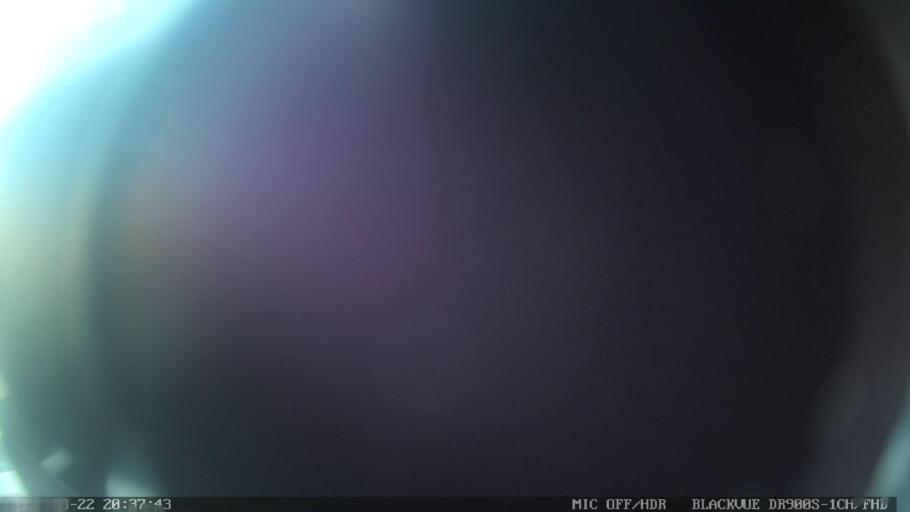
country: PT
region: Portalegre
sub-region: Nisa
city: Nisa
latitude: 39.6769
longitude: -7.7381
